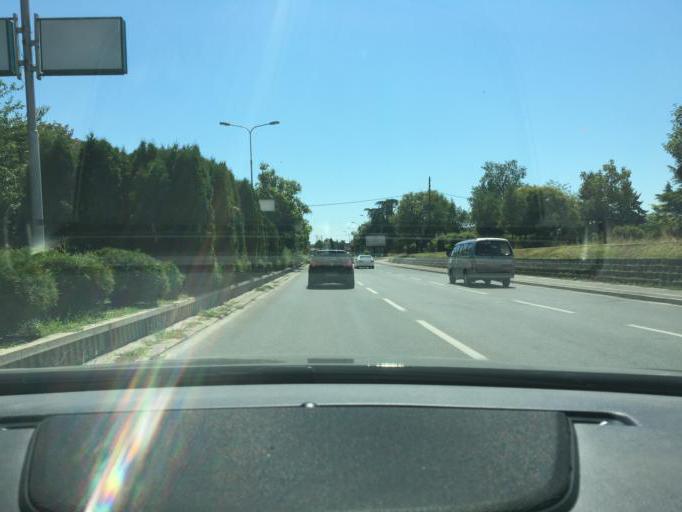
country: MK
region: Karpos
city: Skopje
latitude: 41.9977
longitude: 21.4464
